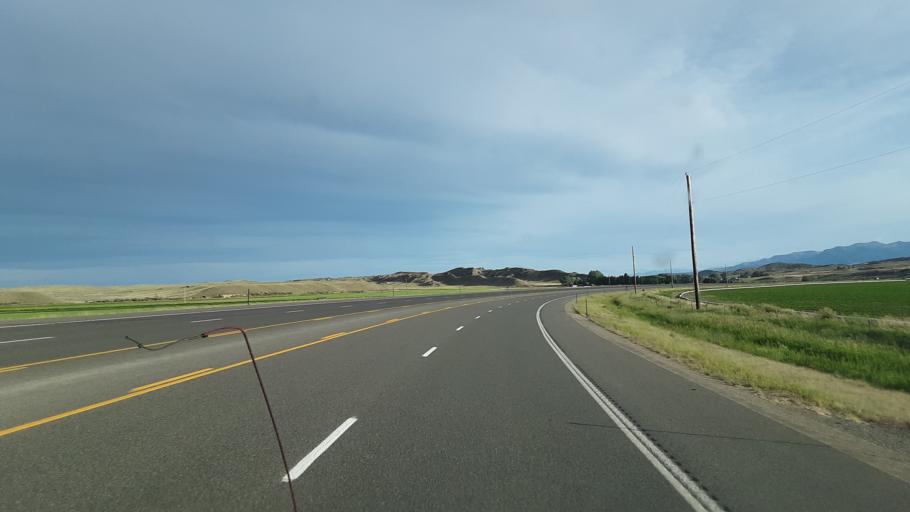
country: US
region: Wyoming
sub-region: Park County
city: Cody
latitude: 44.5522
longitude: -108.9807
